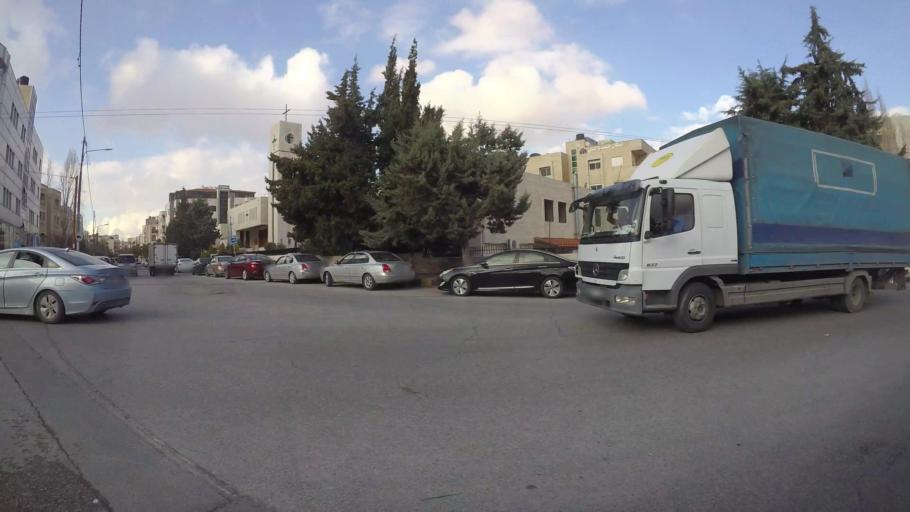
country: JO
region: Amman
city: Wadi as Sir
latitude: 31.9793
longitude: 35.8503
